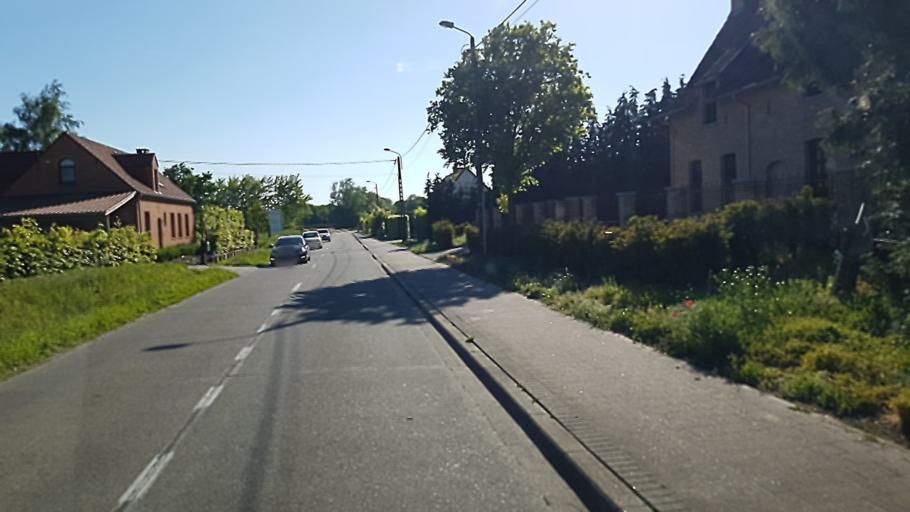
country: BE
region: Flanders
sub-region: Provincie Antwerpen
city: Heist-op-den-Berg
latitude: 51.0930
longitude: 4.6982
